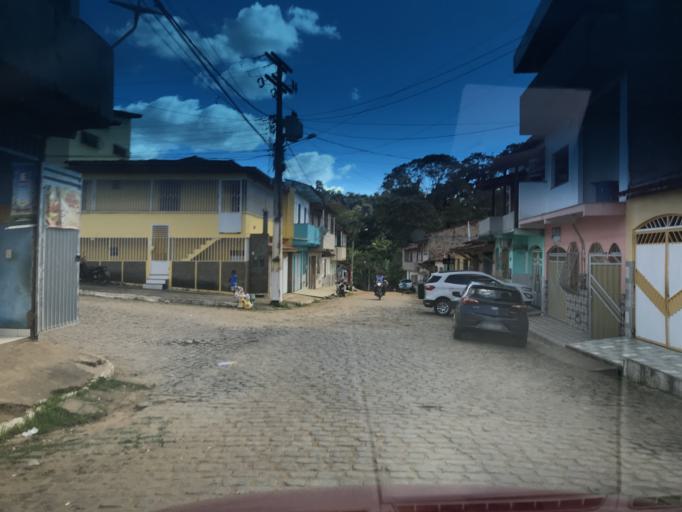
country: BR
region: Bahia
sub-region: Gandu
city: Gandu
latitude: -13.7458
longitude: -39.4944
